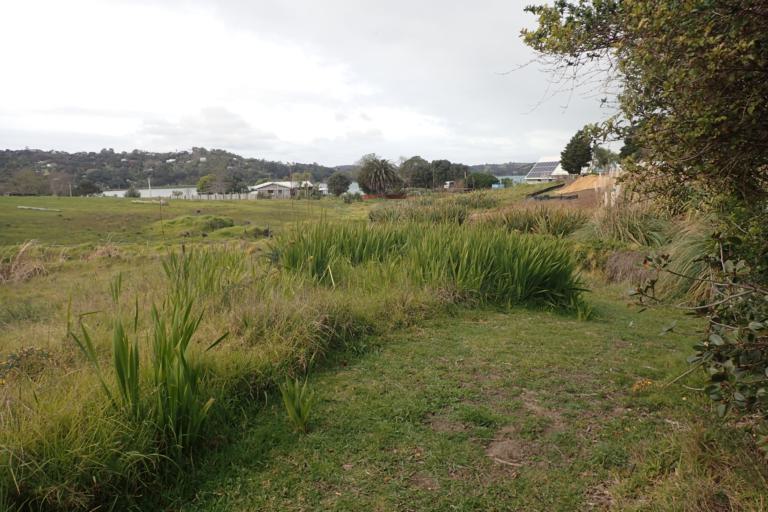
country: NZ
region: Auckland
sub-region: Auckland
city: Pakuranga
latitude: -36.7891
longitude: 175.0062
